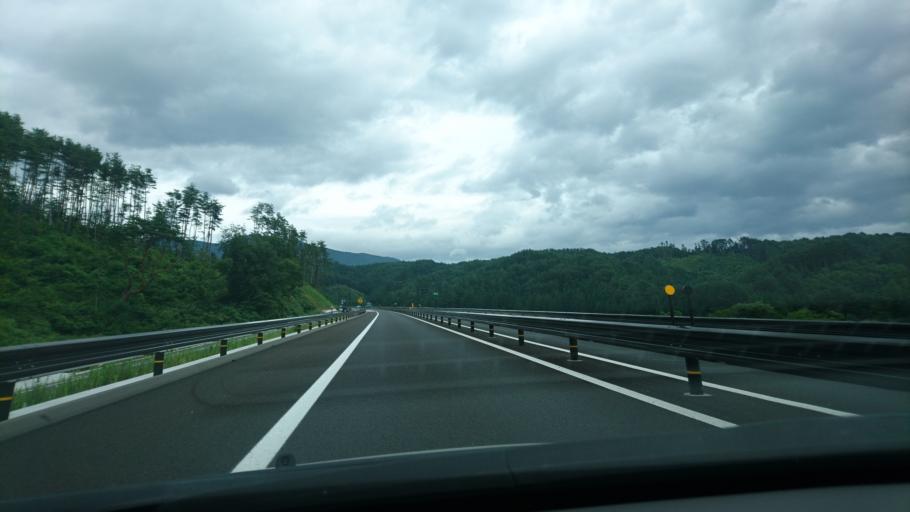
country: JP
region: Iwate
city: Yamada
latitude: 39.4815
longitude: 141.9501
